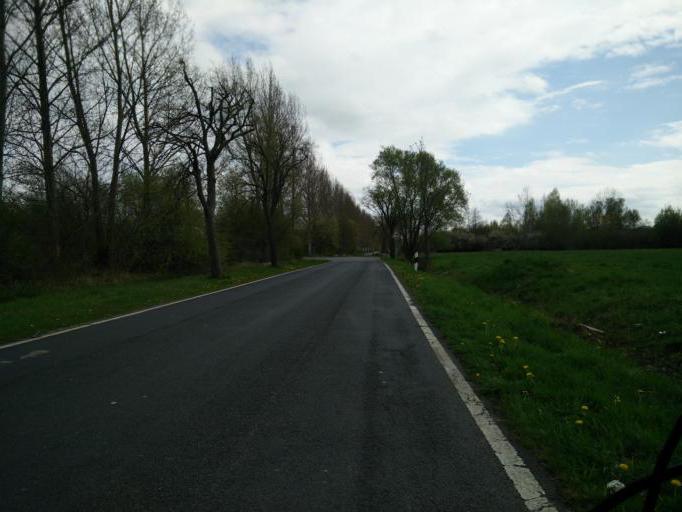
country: DE
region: Mecklenburg-Vorpommern
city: Nienhagen
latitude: 54.1329
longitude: 12.1642
